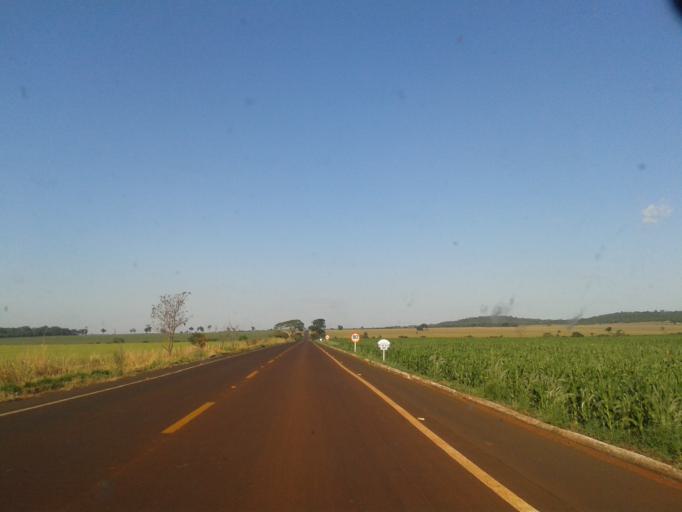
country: BR
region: Minas Gerais
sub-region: Capinopolis
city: Capinopolis
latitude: -18.7121
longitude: -49.8243
